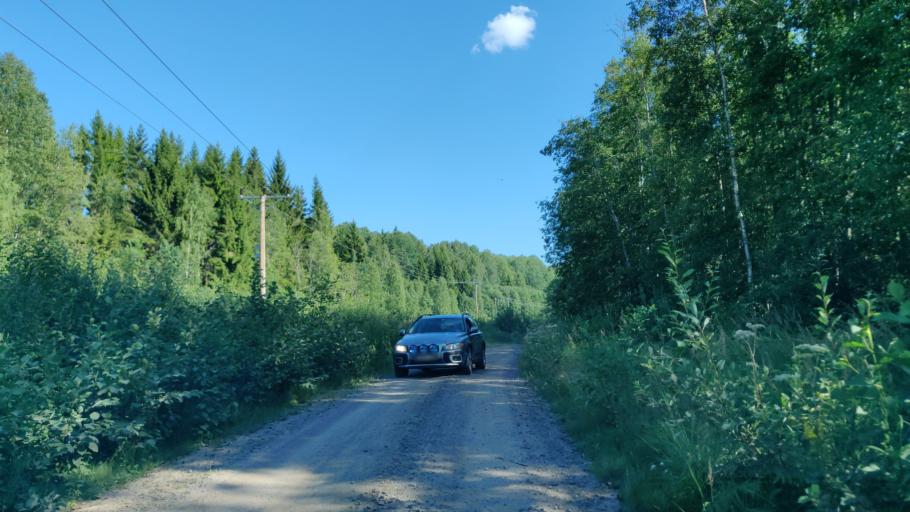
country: SE
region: Vaermland
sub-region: Hagfors Kommun
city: Ekshaerad
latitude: 60.0483
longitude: 13.5246
